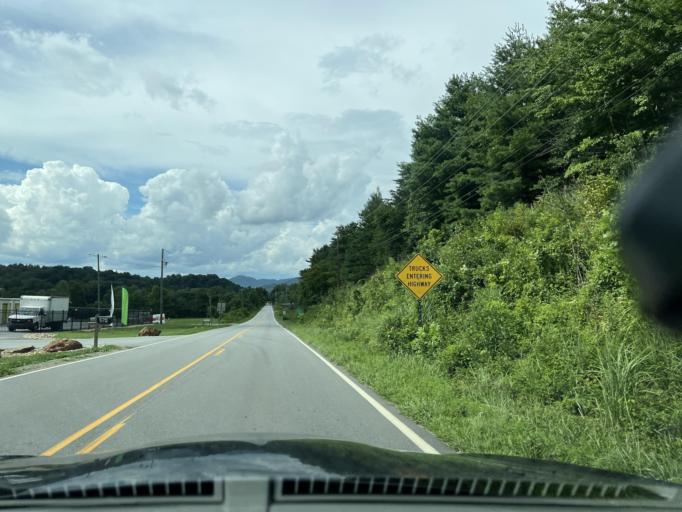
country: US
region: North Carolina
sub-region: Henderson County
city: Hoopers Creek
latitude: 35.4430
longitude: -82.4759
